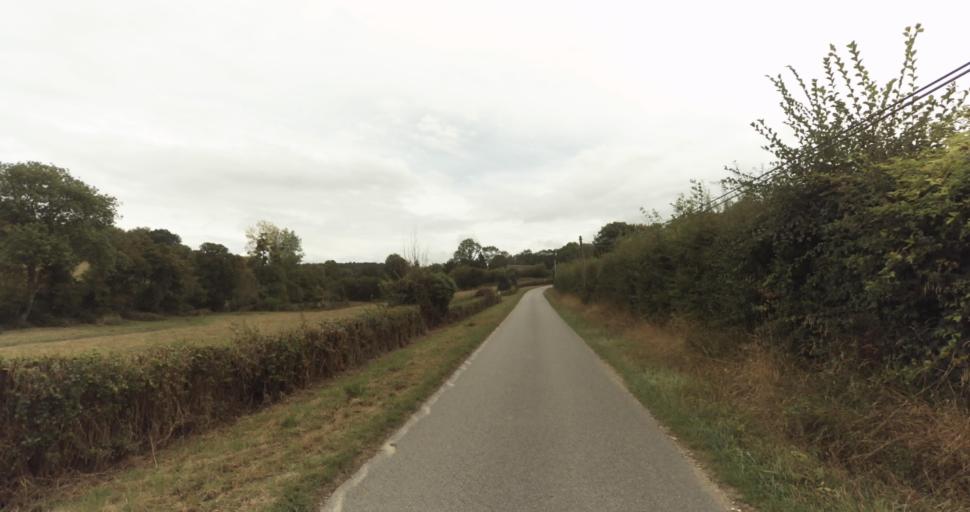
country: FR
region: Lower Normandy
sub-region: Departement de l'Orne
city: Gace
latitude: 48.8268
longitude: 0.2839
